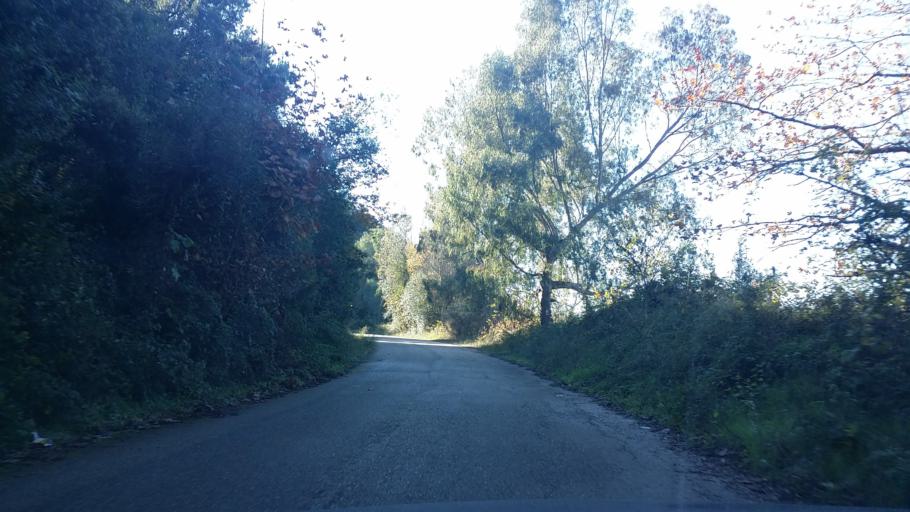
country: GR
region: West Greece
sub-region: Nomos Aitolias kai Akarnanias
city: Krikellos
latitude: 38.9629
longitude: 21.1978
